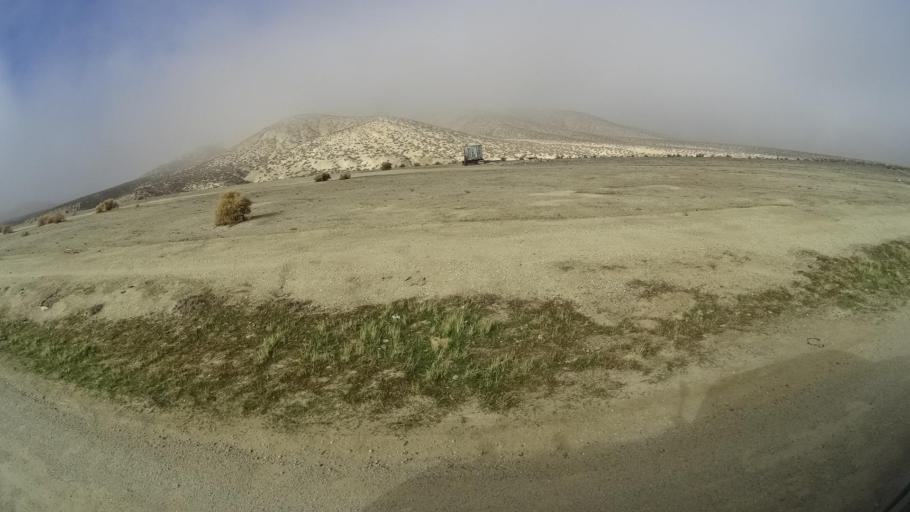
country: US
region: California
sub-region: Kern County
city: Maricopa
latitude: 35.0361
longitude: -119.4348
